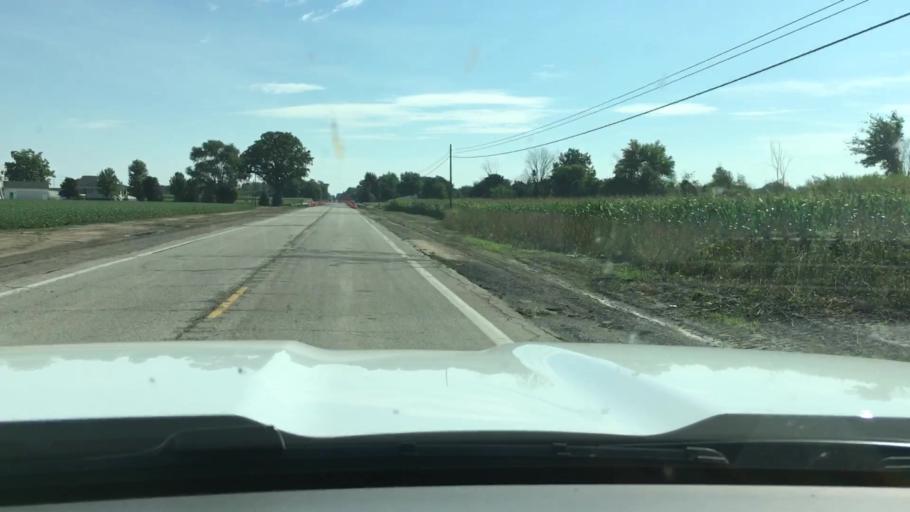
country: US
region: Michigan
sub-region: Saginaw County
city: Hemlock
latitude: 43.4123
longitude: -84.2790
